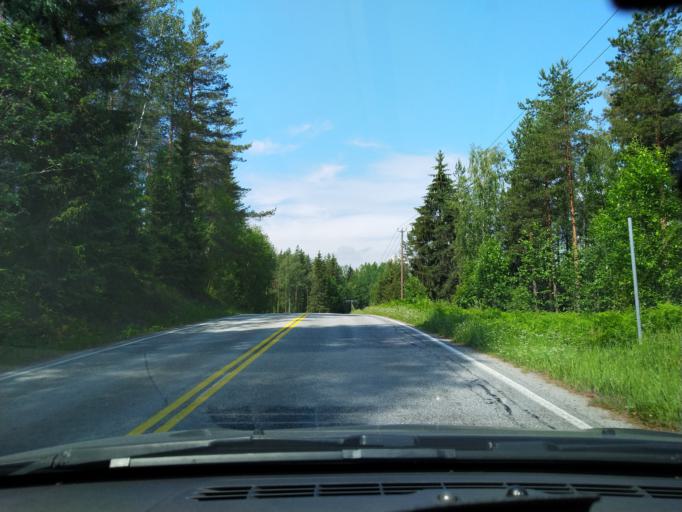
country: FI
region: Uusimaa
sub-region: Helsinki
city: Lohja
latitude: 60.2868
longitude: 24.1051
